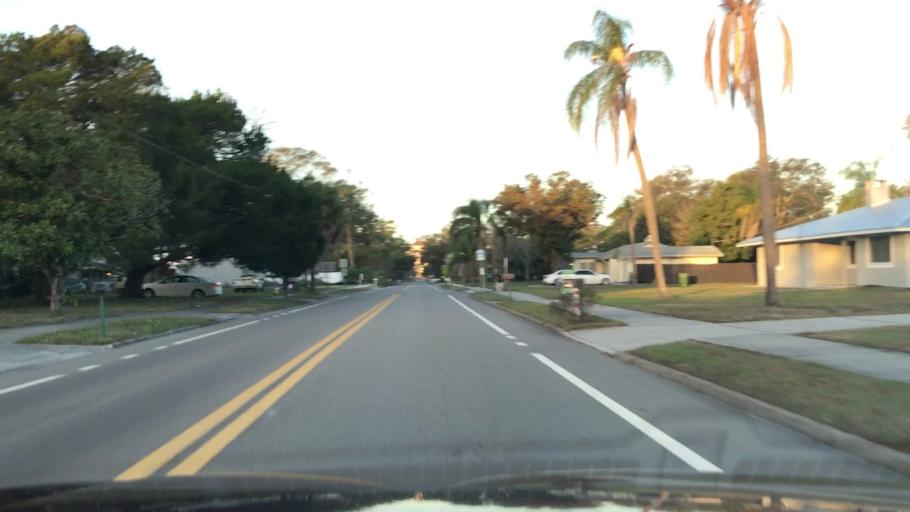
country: US
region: Florida
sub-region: Sarasota County
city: Sarasota
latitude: 27.3365
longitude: -82.5154
